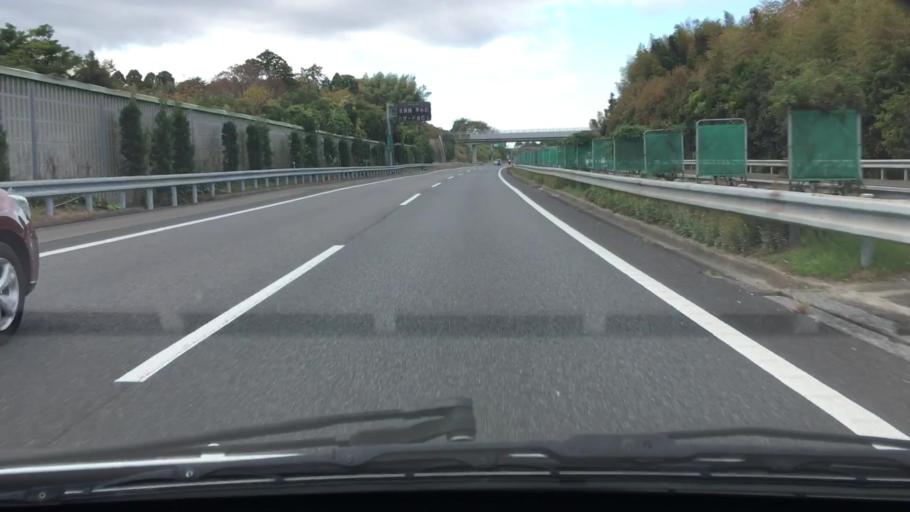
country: JP
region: Chiba
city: Ichihara
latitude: 35.4313
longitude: 140.0484
